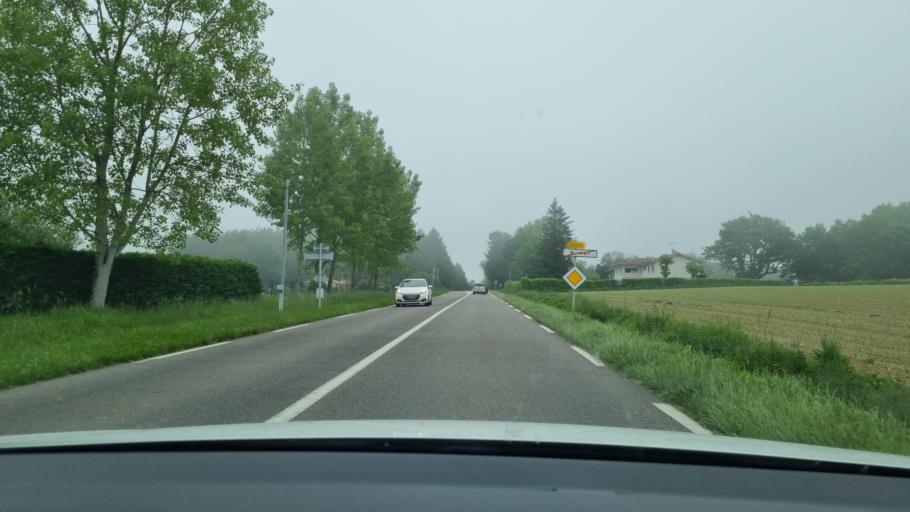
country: FR
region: Aquitaine
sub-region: Departement des Landes
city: Hagetmau
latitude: 43.6206
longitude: -0.6307
